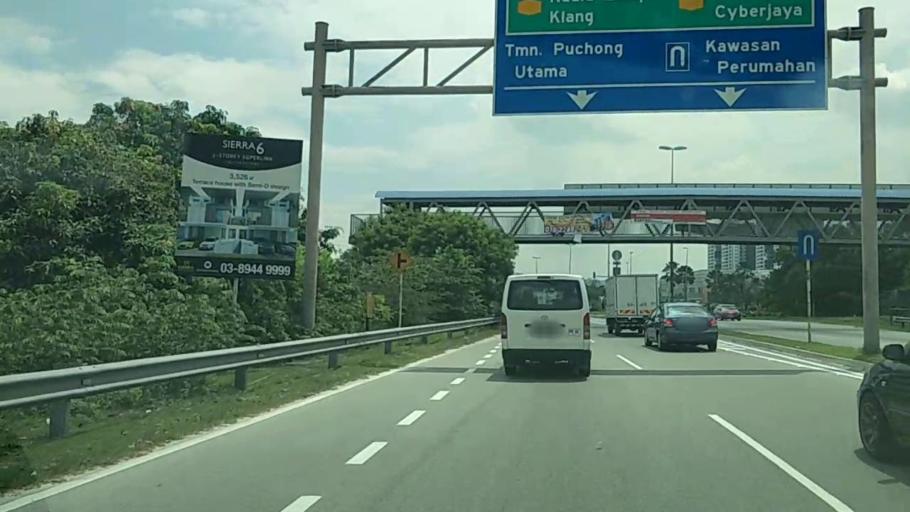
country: MY
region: Selangor
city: Subang Jaya
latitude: 2.9808
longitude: 101.6150
